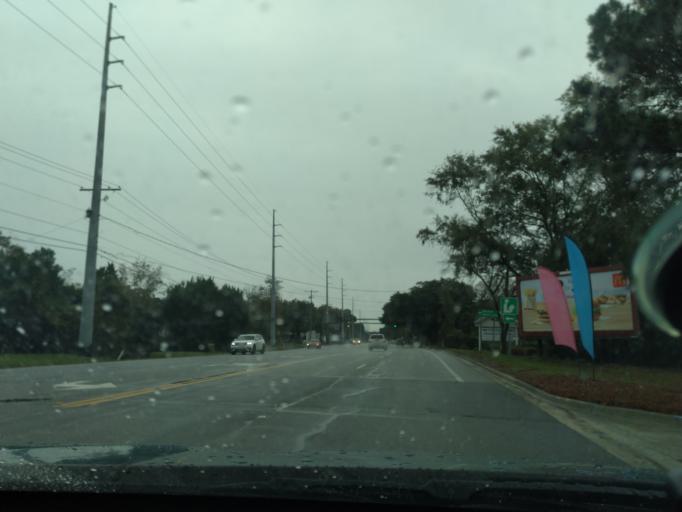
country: US
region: South Carolina
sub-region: Charleston County
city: Folly Beach
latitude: 32.7003
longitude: -79.9673
